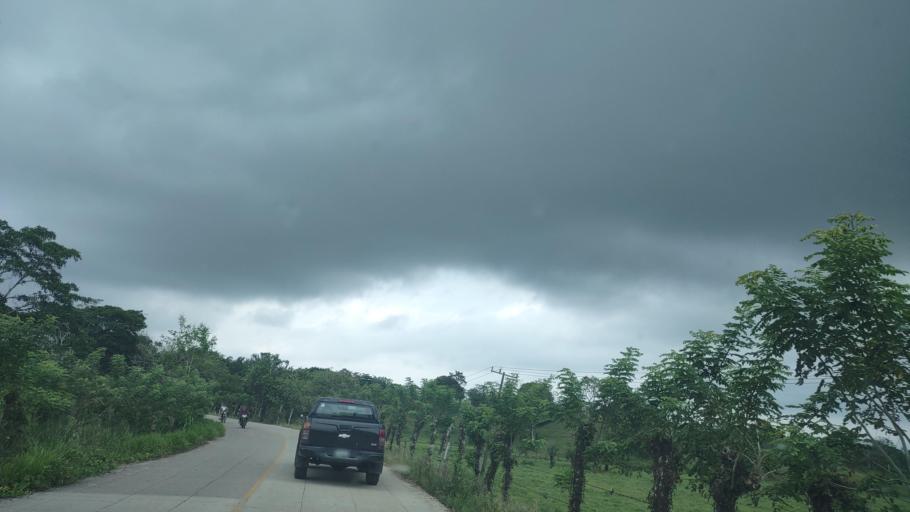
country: MX
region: Veracruz
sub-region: Uxpanapa
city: Poblado 10
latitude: 17.4950
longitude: -94.1722
